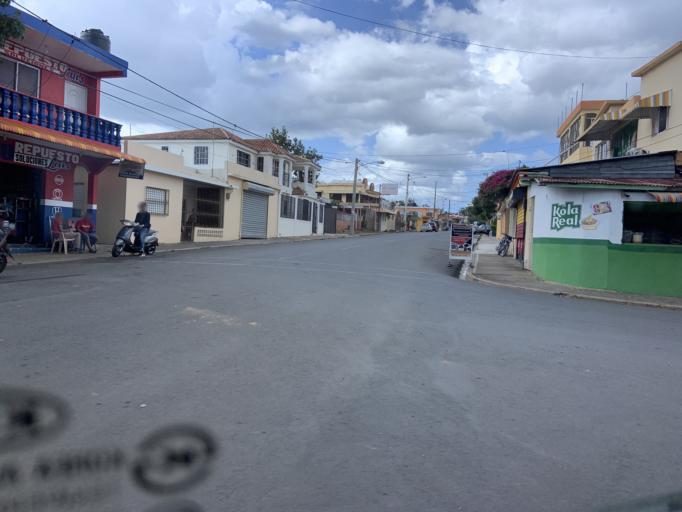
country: DO
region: Monte Plata
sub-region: Yamasa
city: Yamasa
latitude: 18.7662
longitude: -70.0241
